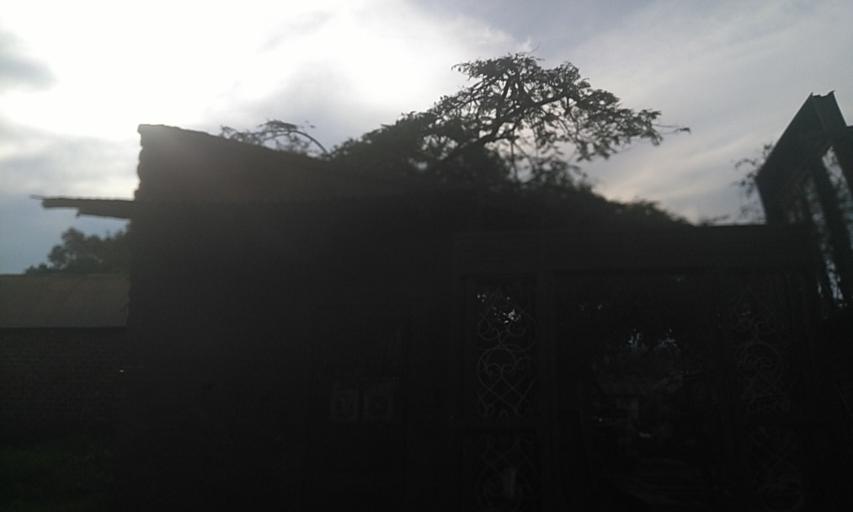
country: UG
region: Central Region
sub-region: Wakiso District
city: Kajansi
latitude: 0.2712
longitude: 32.5131
